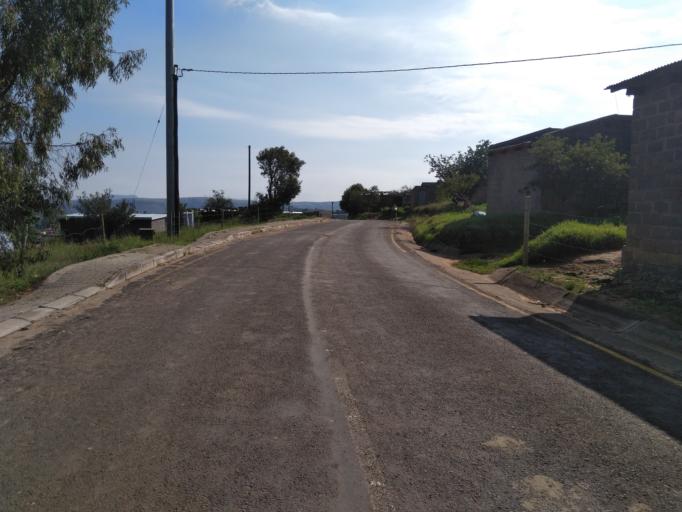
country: LS
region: Butha-Buthe
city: Butha-Buthe
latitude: -28.7756
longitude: 28.2460
